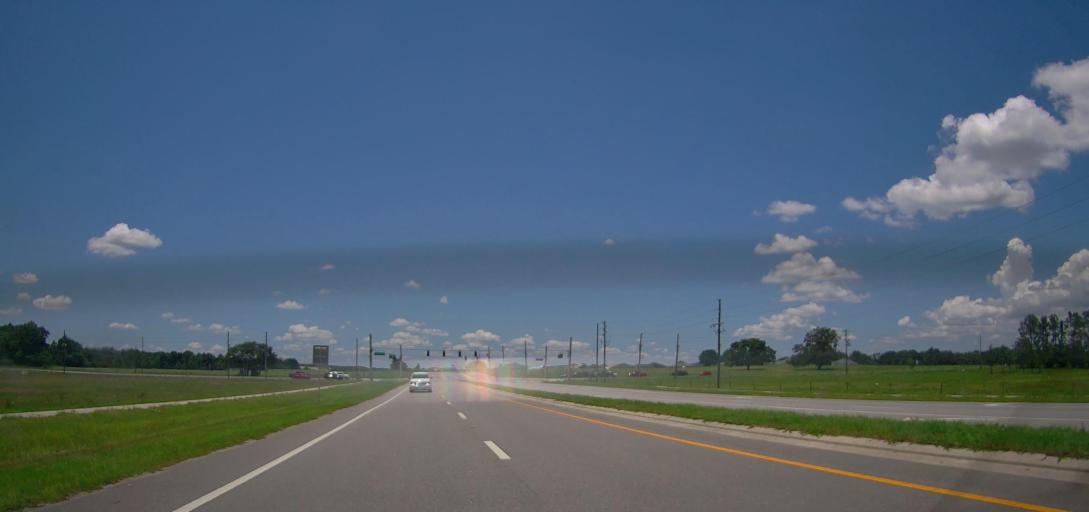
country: US
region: Florida
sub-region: Marion County
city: Belleview
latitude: 29.0862
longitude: -82.0517
